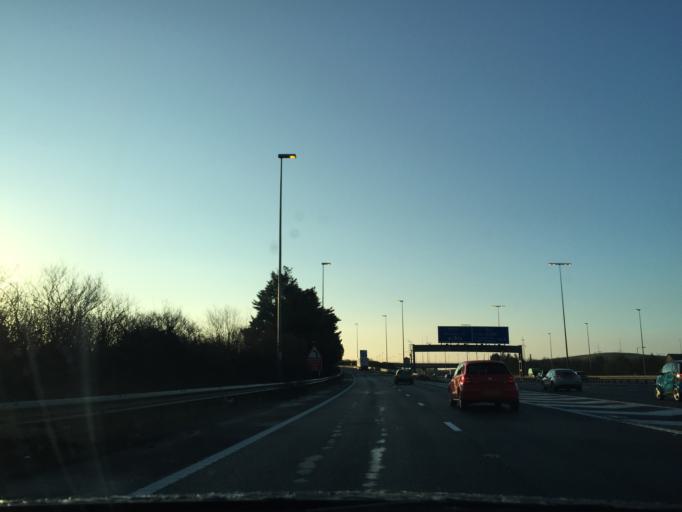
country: GB
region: England
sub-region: Portsmouth
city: Cosham
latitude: 50.8445
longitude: -1.0964
